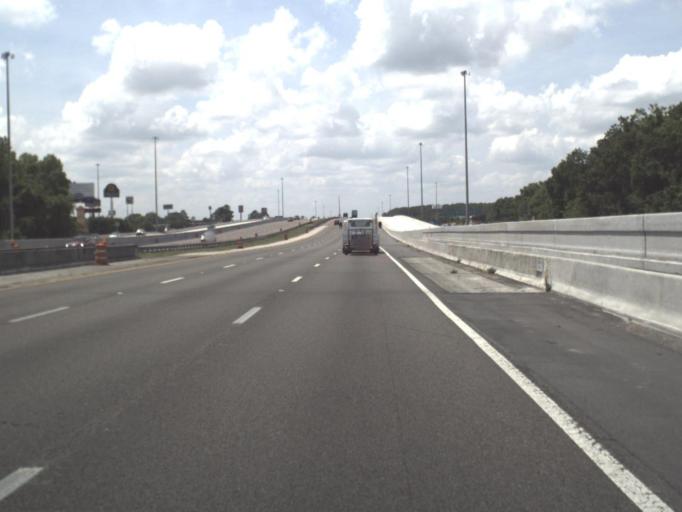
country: US
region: Florida
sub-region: Clay County
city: Bellair-Meadowbrook Terrace
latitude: 30.1946
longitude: -81.7336
